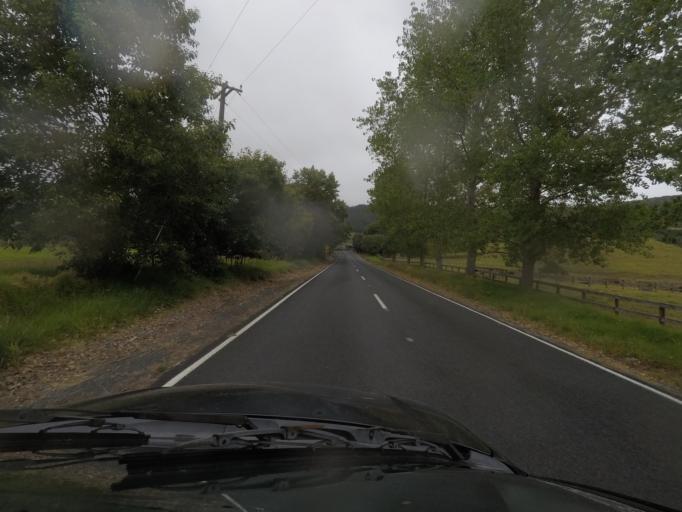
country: NZ
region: Auckland
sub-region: Auckland
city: Warkworth
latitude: -36.2652
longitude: 174.7020
